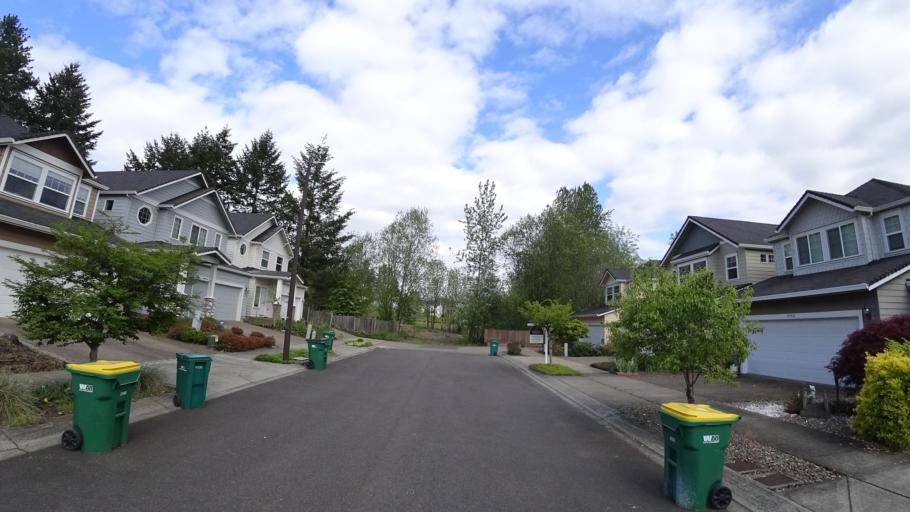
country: US
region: Oregon
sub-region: Washington County
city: Beaverton
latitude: 45.4468
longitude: -122.8279
